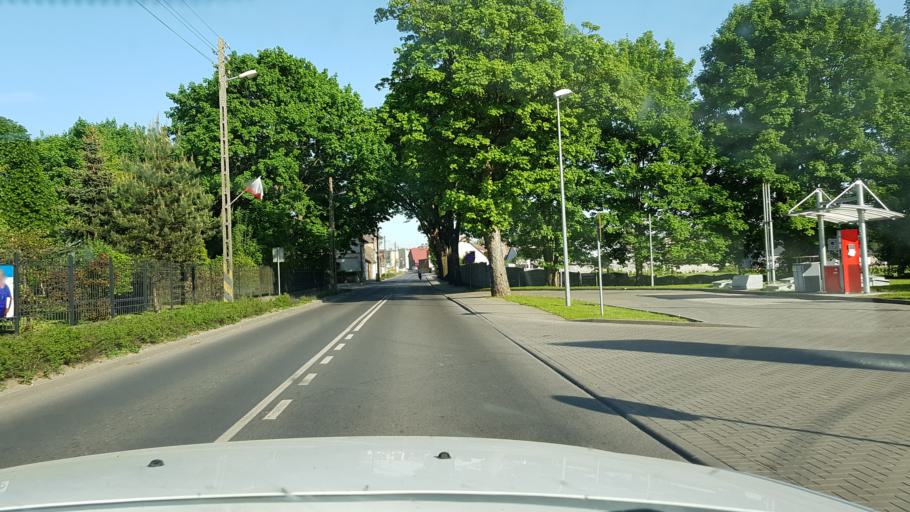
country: PL
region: West Pomeranian Voivodeship
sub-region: Powiat lobeski
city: Resko
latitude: 53.7748
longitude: 15.3994
